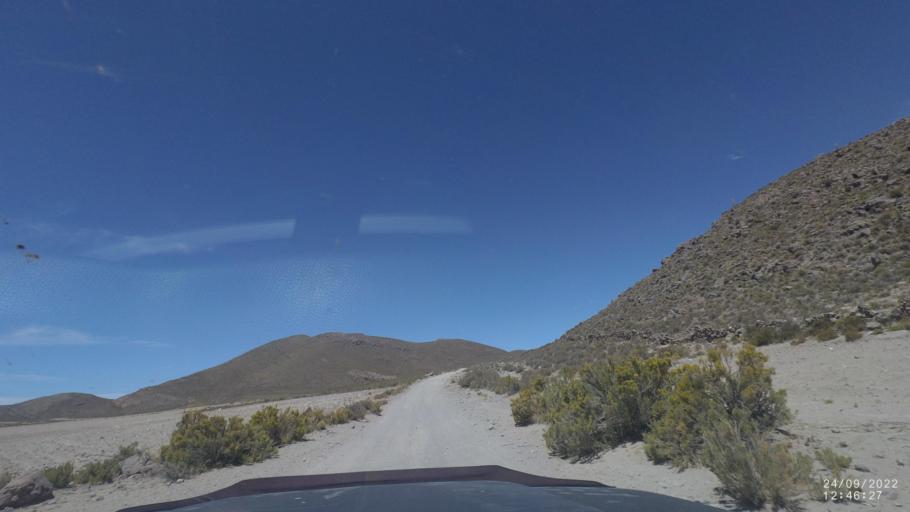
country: BO
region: Potosi
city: Colchani
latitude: -19.8034
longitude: -67.5718
